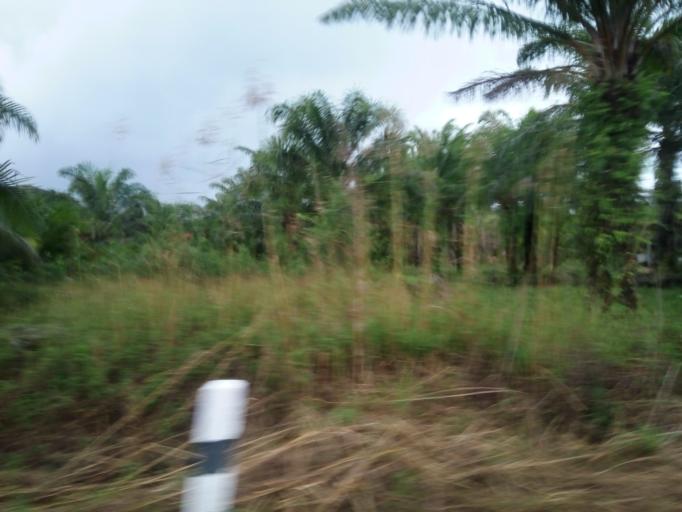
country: TH
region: Phangnga
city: Ban Ao Nang
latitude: 8.1453
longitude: 98.7449
